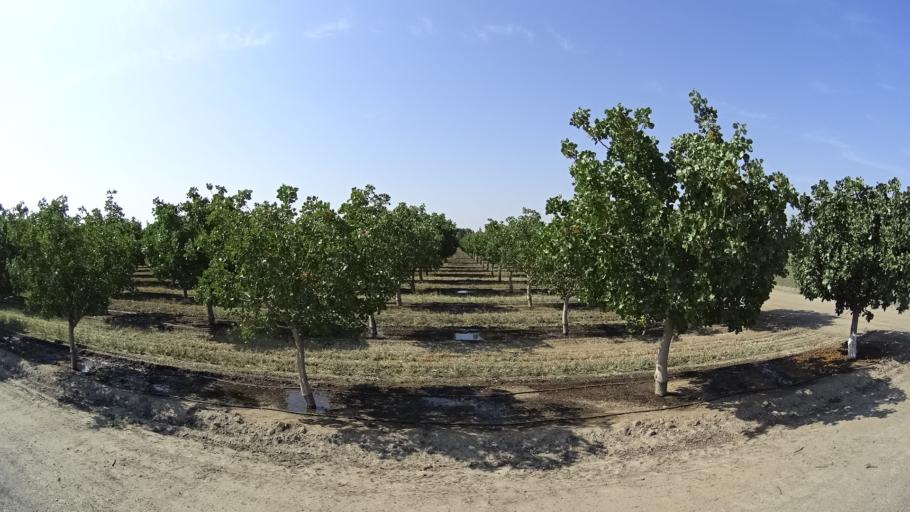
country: US
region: California
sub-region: Kings County
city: Lemoore
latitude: 36.3206
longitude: -119.8257
